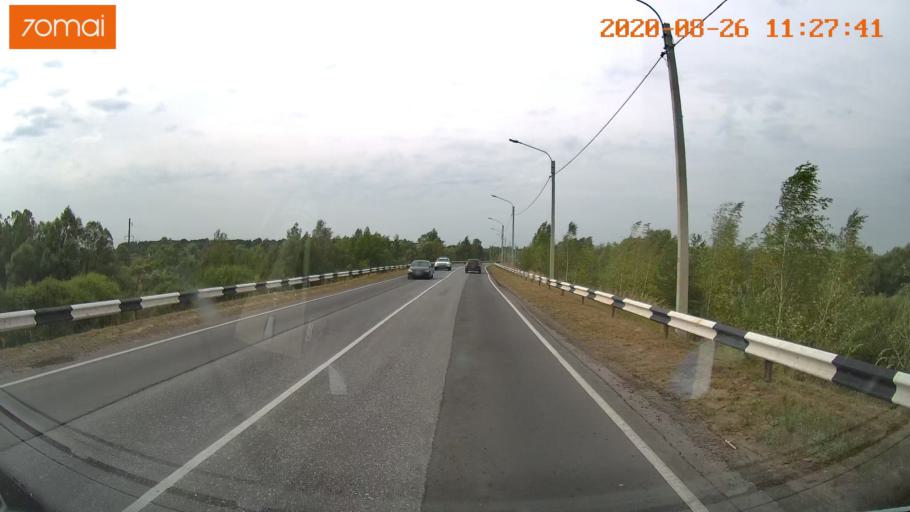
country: RU
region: Rjazan
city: Shilovo
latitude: 54.3258
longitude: 40.9305
